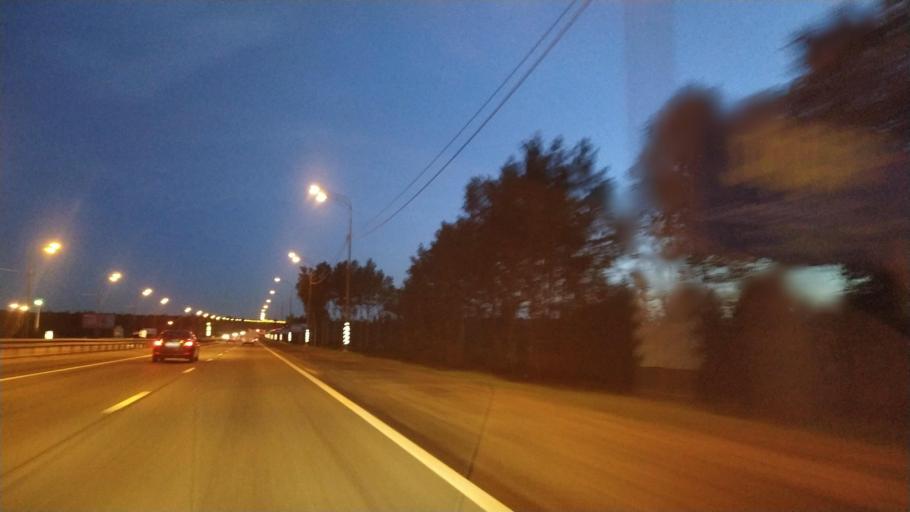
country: RU
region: Leningrad
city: Koltushi
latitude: 59.8926
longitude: 30.6479
